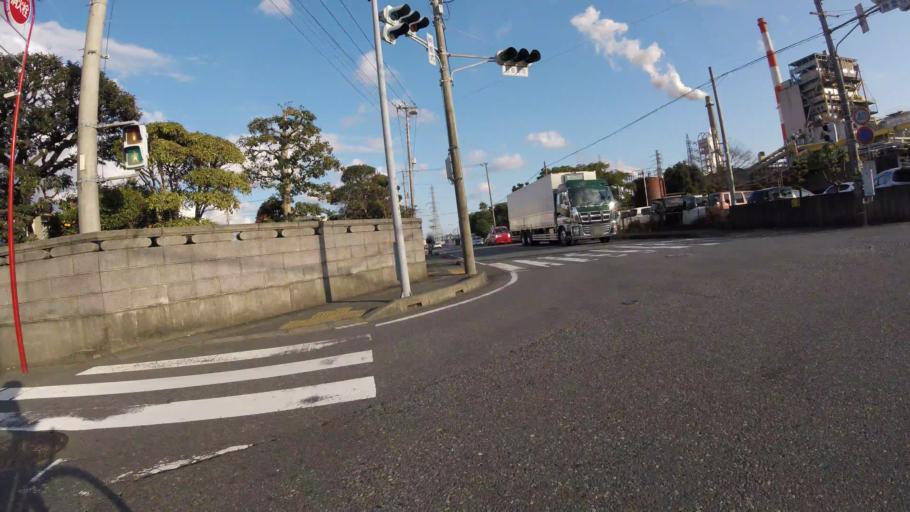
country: JP
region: Shizuoka
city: Fuji
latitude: 35.1527
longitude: 138.6621
